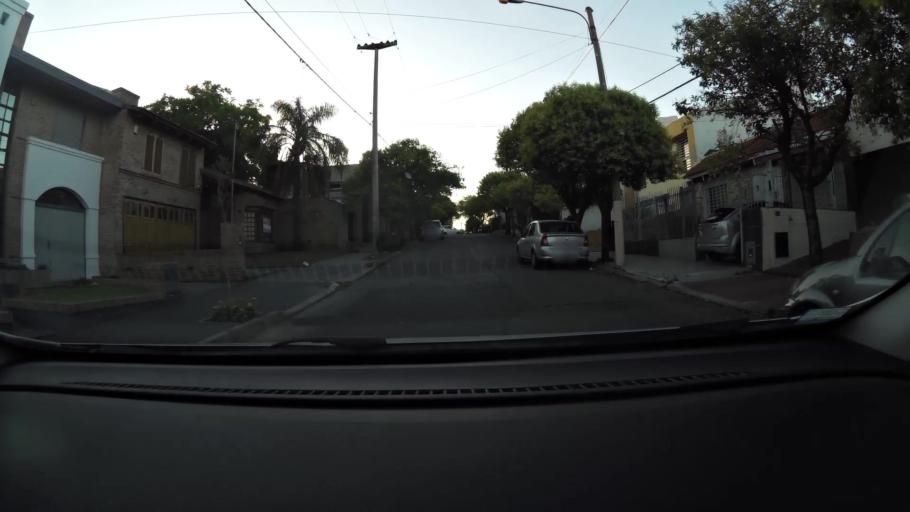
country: AR
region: Cordoba
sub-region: Departamento de Capital
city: Cordoba
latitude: -31.3802
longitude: -64.2174
